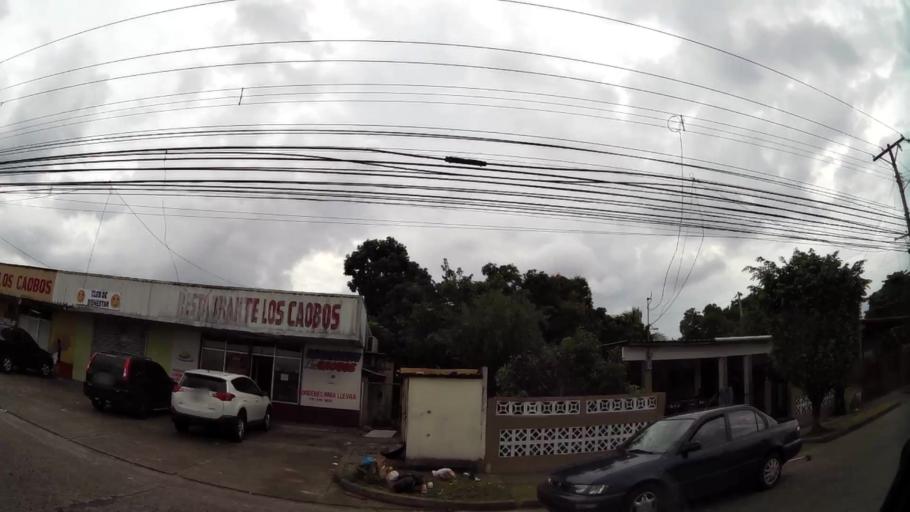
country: PA
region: Panama
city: Tocumen
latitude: 9.0585
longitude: -79.4138
